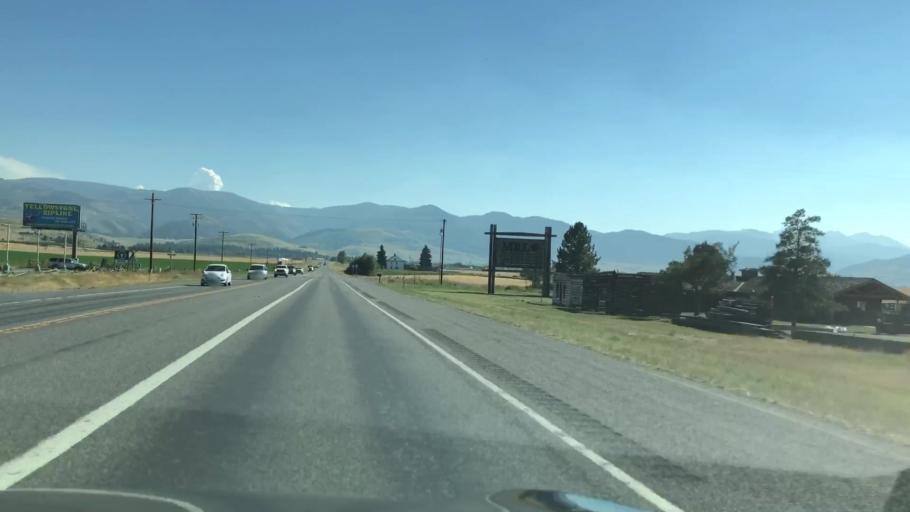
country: US
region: Montana
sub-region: Gallatin County
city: Four Corners
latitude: 45.5855
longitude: -111.1978
